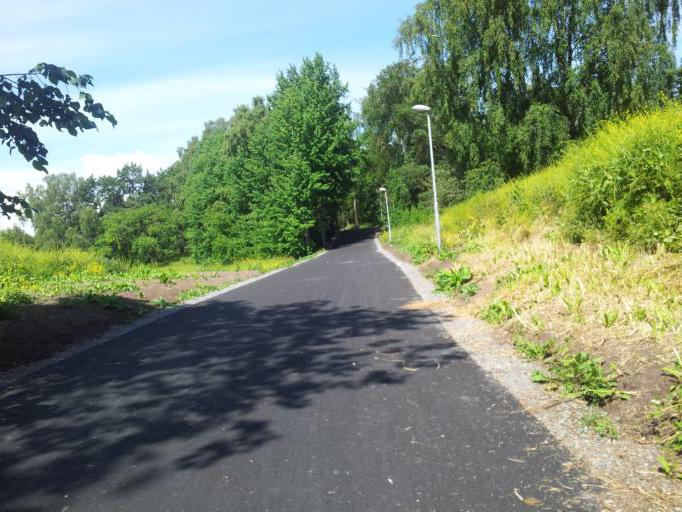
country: SE
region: Uppsala
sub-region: Uppsala Kommun
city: Uppsala
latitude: 59.8543
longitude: 17.6735
